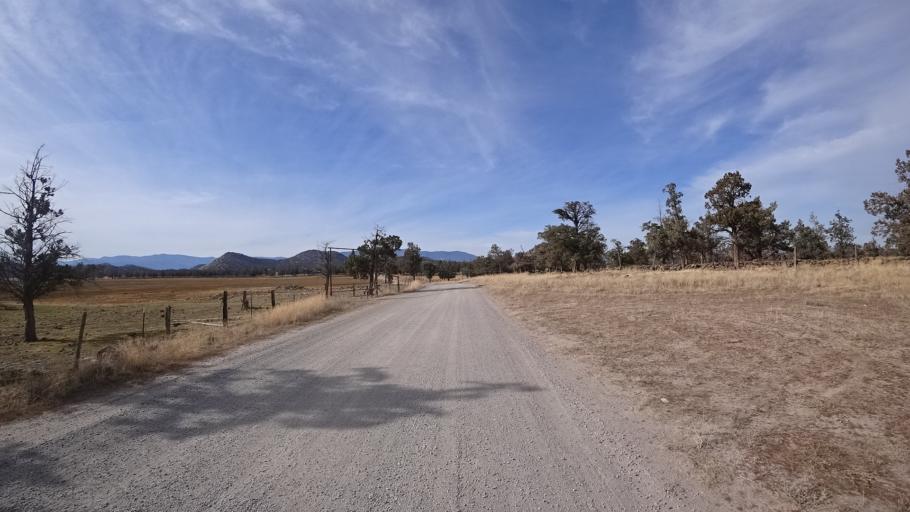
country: US
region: California
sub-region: Siskiyou County
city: Montague
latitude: 41.5953
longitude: -122.4190
